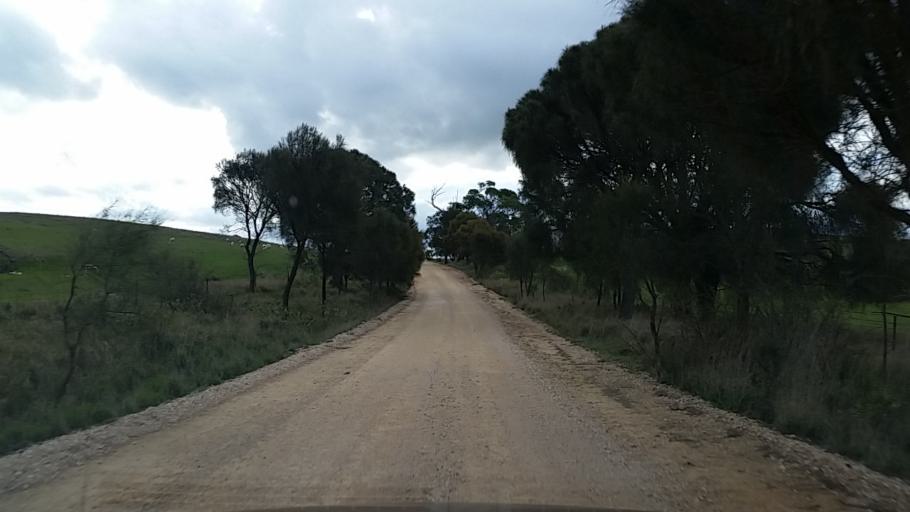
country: AU
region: South Australia
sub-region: Mount Barker
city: Callington
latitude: -34.9724
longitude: 139.0563
